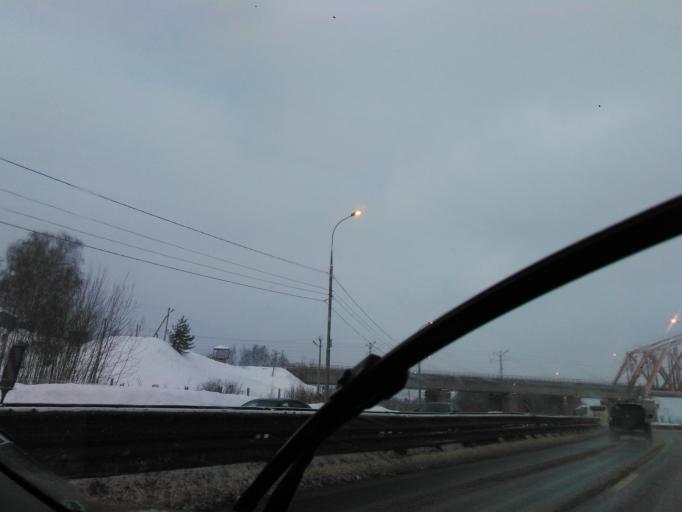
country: RU
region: Moskovskaya
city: Dedenevo
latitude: 56.2573
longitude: 37.5105
